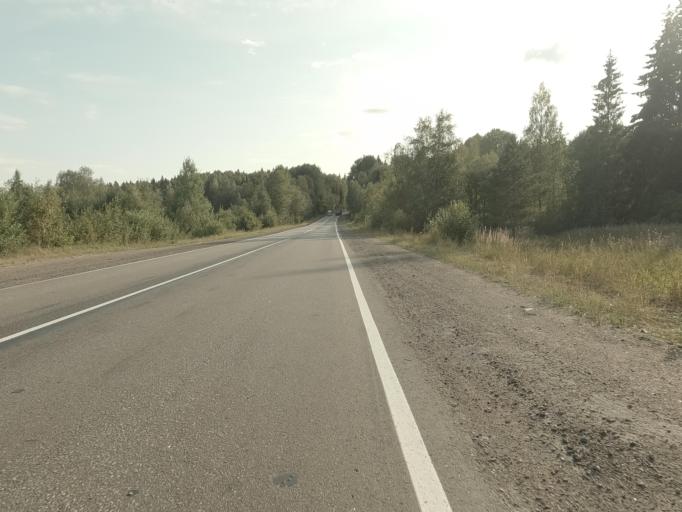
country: RU
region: Leningrad
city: Vyborg
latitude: 60.8449
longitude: 28.8549
